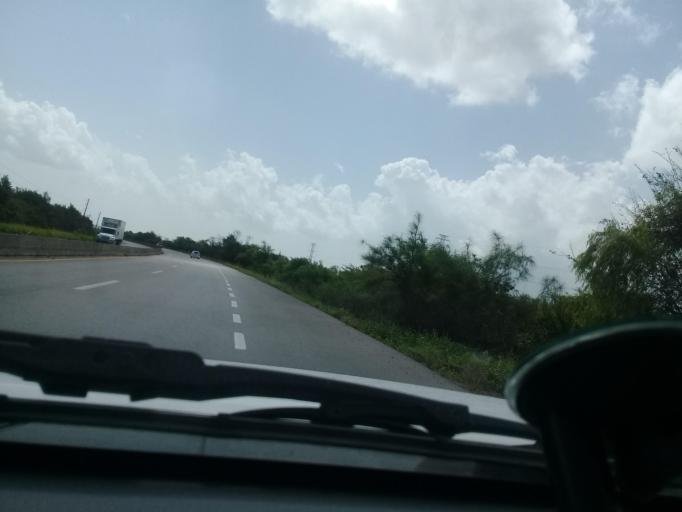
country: MX
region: Veracruz
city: Moralillo
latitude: 22.2117
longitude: -97.9631
